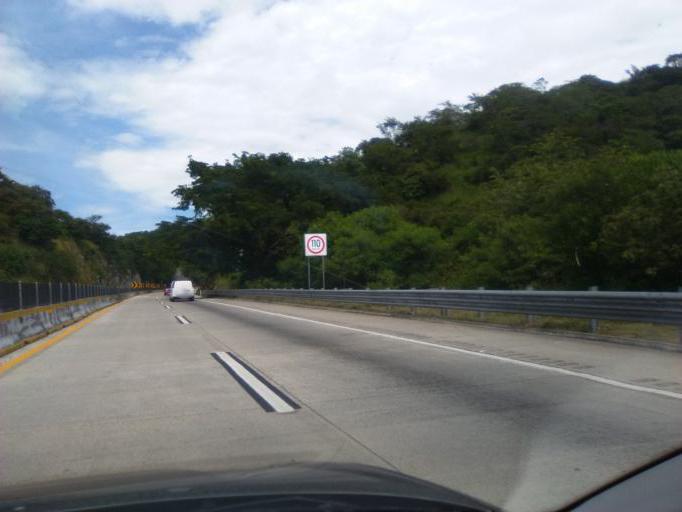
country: MX
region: Guerrero
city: Tierra Colorada
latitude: 17.1833
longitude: -99.5516
